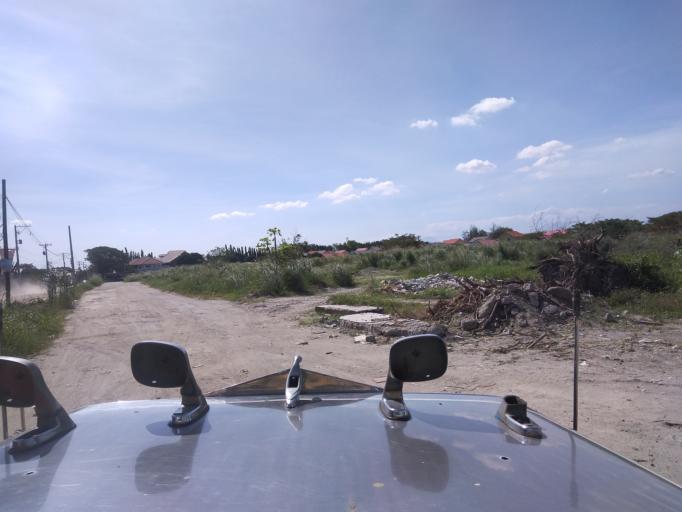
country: PH
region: Central Luzon
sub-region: Province of Pampanga
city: Magliman
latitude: 15.0405
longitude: 120.6594
